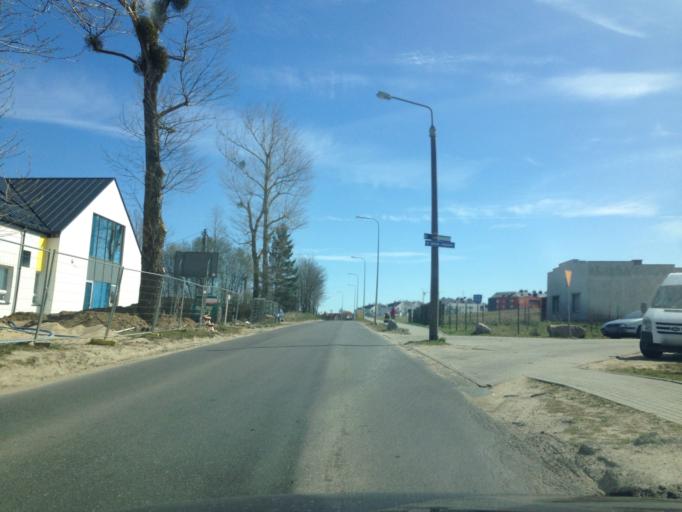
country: PL
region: Pomeranian Voivodeship
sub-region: Powiat wejherowski
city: Bojano
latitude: 54.4898
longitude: 18.4250
